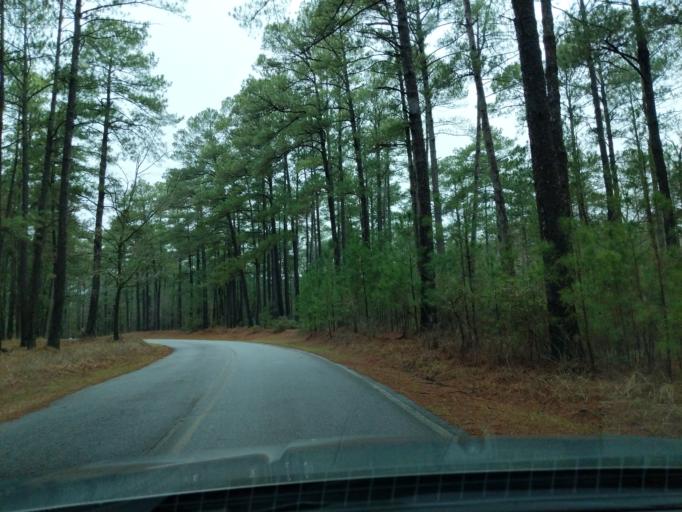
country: US
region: Georgia
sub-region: Columbia County
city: Appling
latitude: 33.6506
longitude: -82.3738
